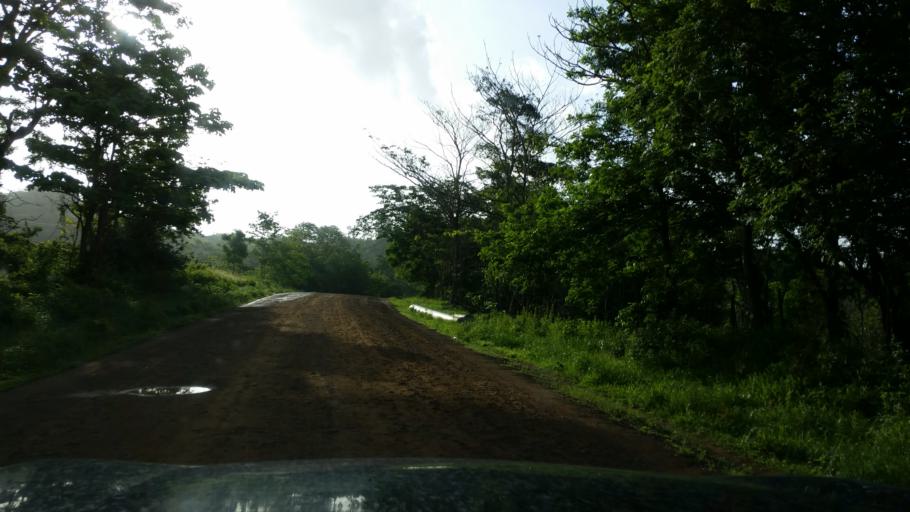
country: NI
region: Atlantico Norte (RAAN)
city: Puerto Cabezas
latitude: 14.0685
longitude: -83.9761
